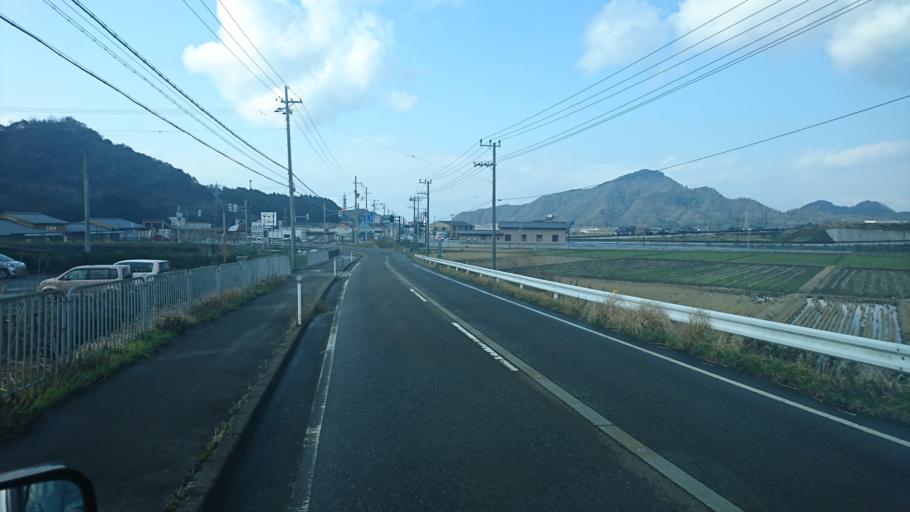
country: JP
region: Tottori
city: Tottori
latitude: 35.6096
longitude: 134.4712
